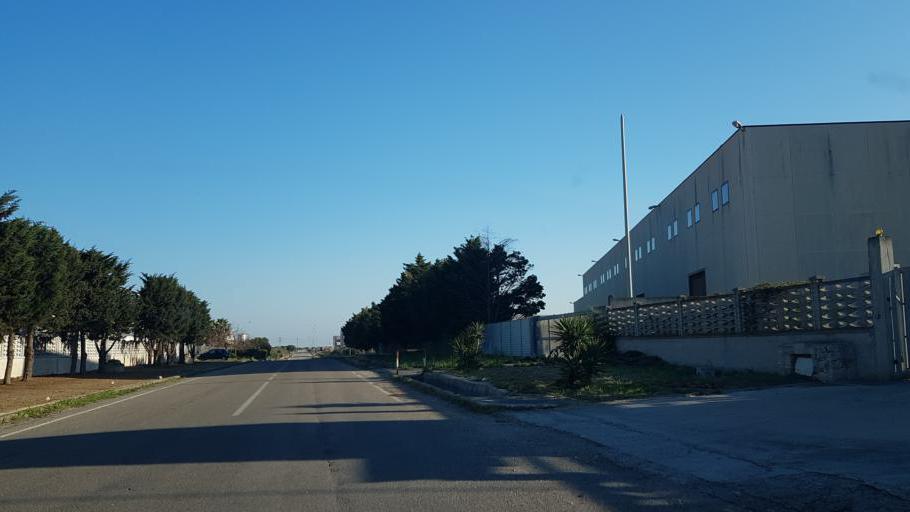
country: IT
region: Apulia
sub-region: Provincia di Brindisi
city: La Rosa
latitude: 40.6274
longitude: 17.9691
